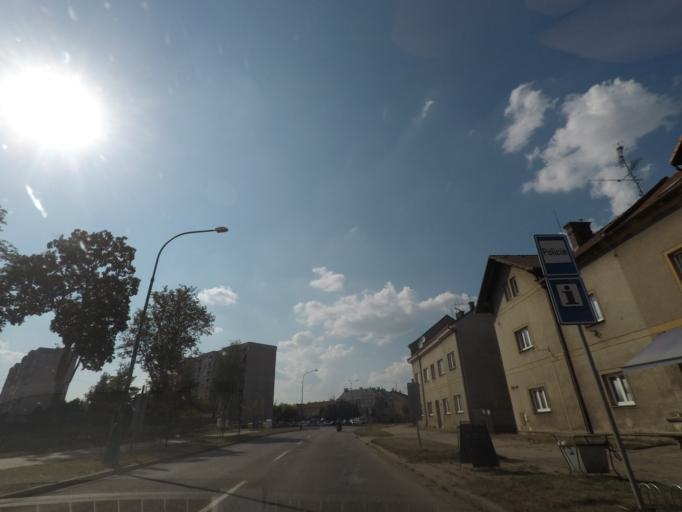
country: CZ
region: Kralovehradecky
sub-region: Okres Nachod
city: Jaromer
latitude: 50.3457
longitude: 15.9177
